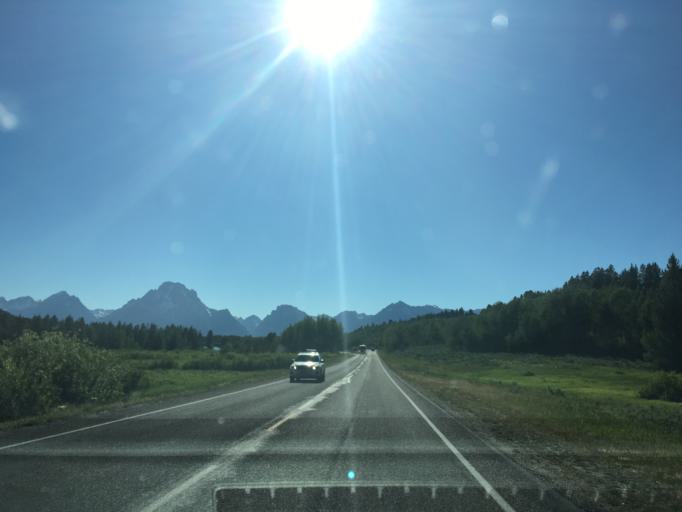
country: US
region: Wyoming
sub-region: Teton County
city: Jackson
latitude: 43.8659
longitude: -110.5441
